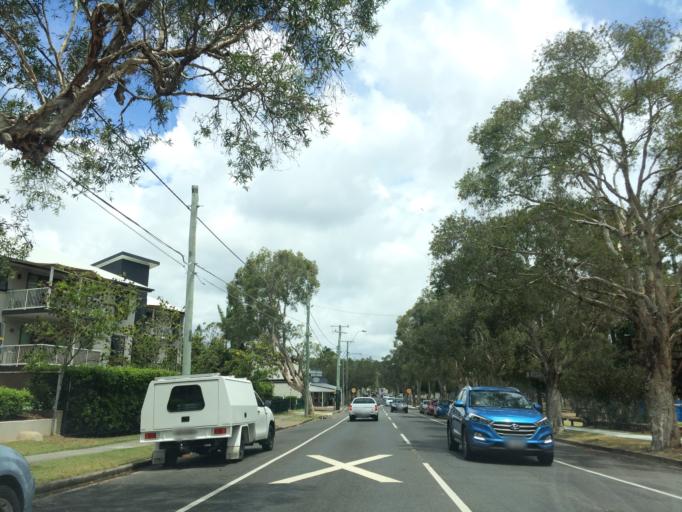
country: AU
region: Queensland
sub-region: Brisbane
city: Balmoral
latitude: -27.4628
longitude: 153.0637
